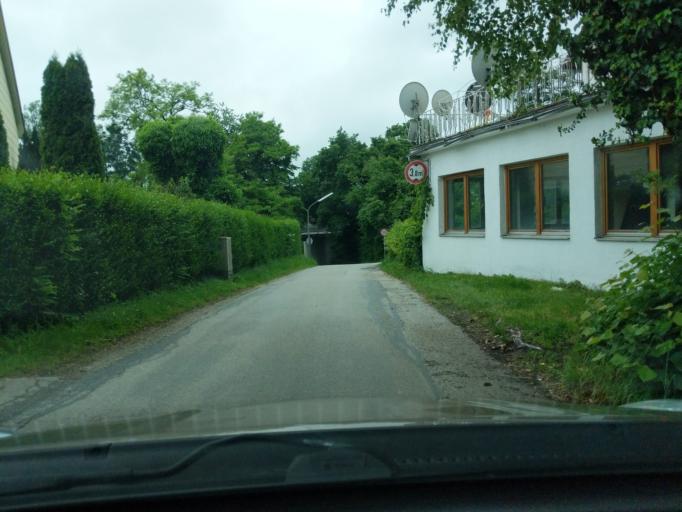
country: DE
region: Bavaria
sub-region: Upper Bavaria
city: Kirchseeon
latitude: 48.0711
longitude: 11.9099
